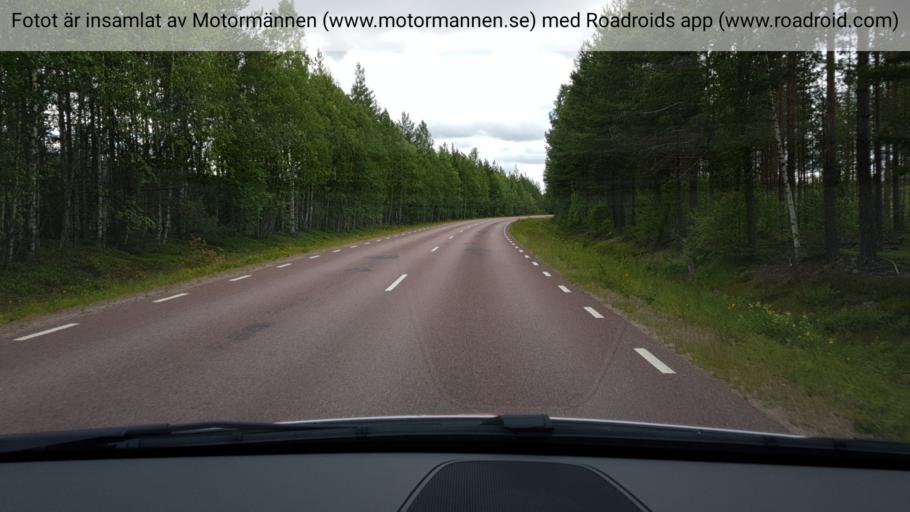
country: SE
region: Jaemtland
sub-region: Harjedalens Kommun
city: Sveg
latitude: 62.0034
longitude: 14.2883
